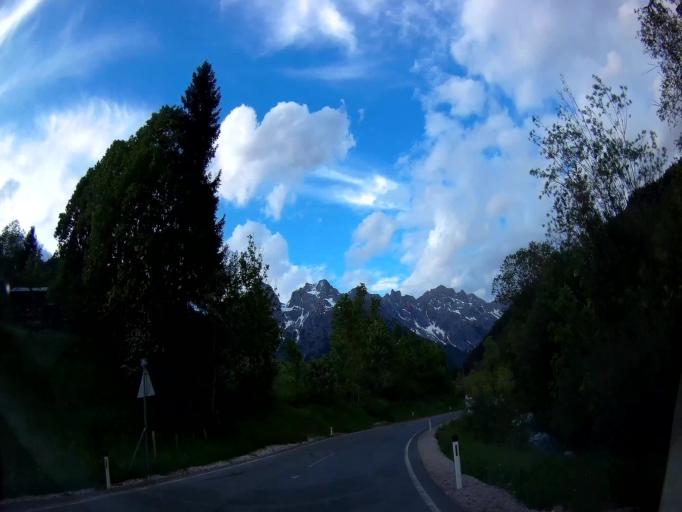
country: AT
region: Salzburg
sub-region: Politischer Bezirk Zell am See
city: Dienten am Hochkonig
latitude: 47.3958
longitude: 12.9603
